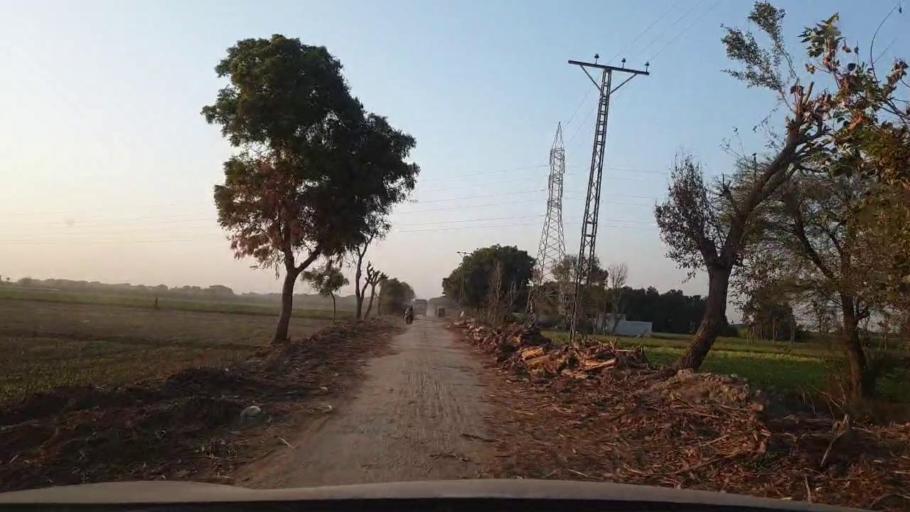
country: PK
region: Sindh
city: Tando Allahyar
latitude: 25.4907
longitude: 68.7459
